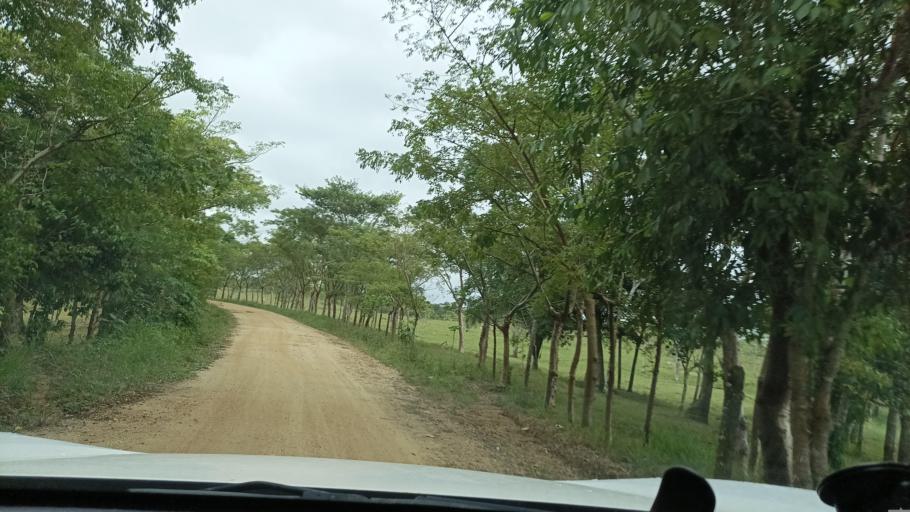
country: MX
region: Veracruz
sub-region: Moloacan
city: Cuichapa
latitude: 17.7921
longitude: -94.3702
